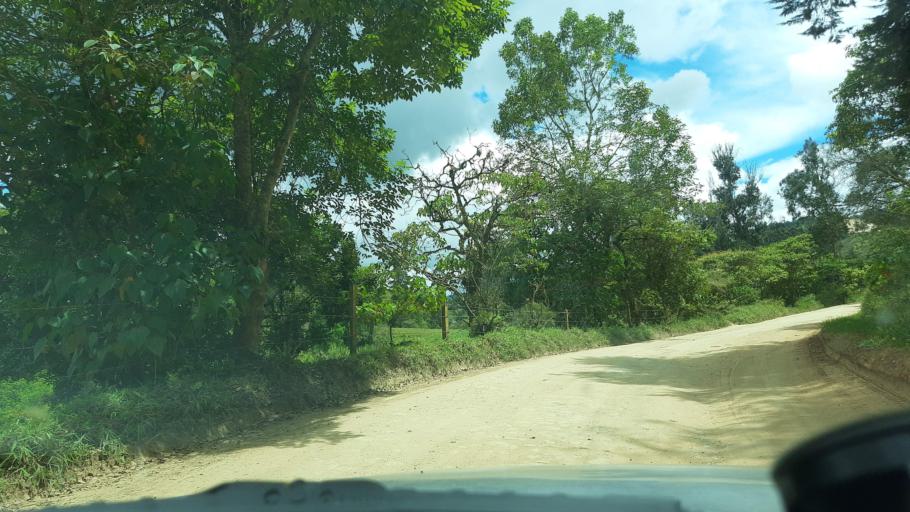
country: CO
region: Cundinamarca
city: Umbita
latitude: 5.2207
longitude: -73.4285
